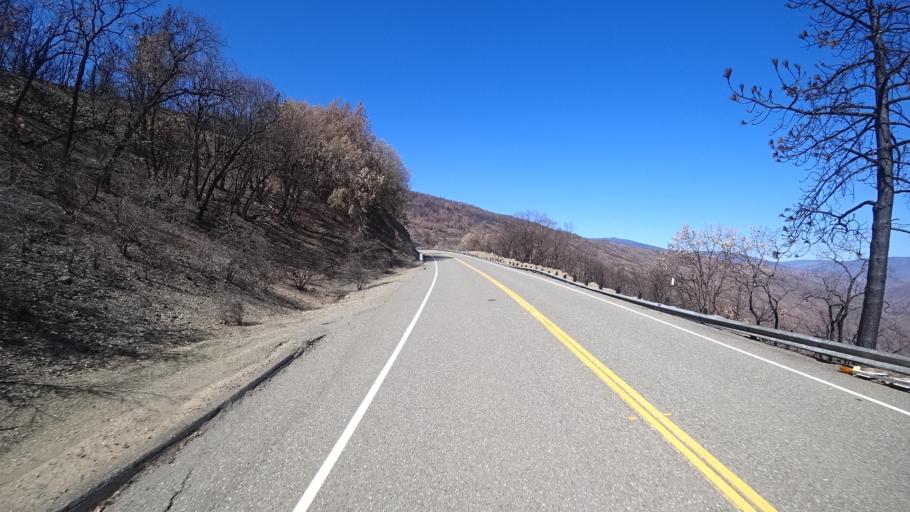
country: US
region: California
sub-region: Tehama County
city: Rancho Tehama Reserve
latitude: 39.6676
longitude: -122.6751
